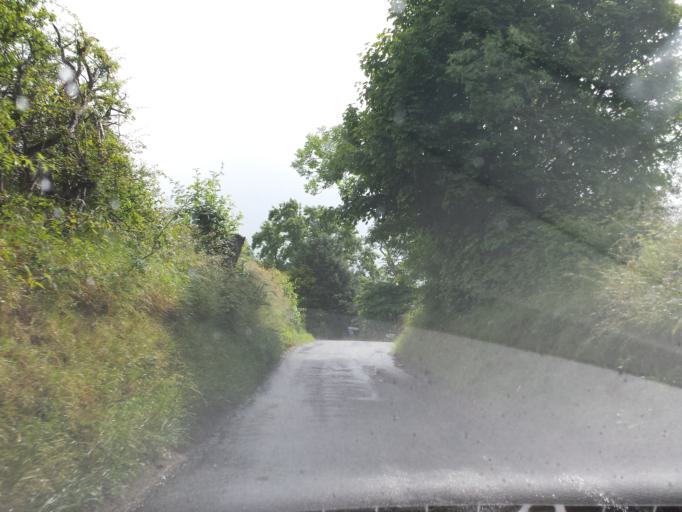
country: GB
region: Scotland
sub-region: The Scottish Borders
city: Saint Boswells
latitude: 55.5953
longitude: -2.6420
